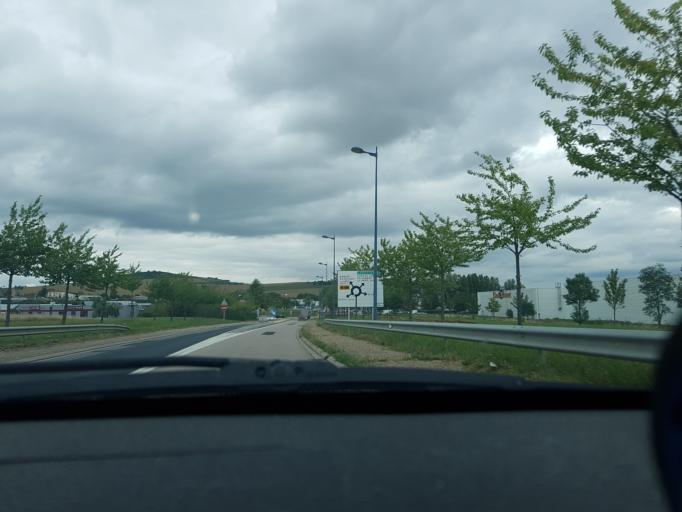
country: FR
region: Lorraine
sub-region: Departement de Meurthe-et-Moselle
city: Pulnoy
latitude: 48.7061
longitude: 6.2426
